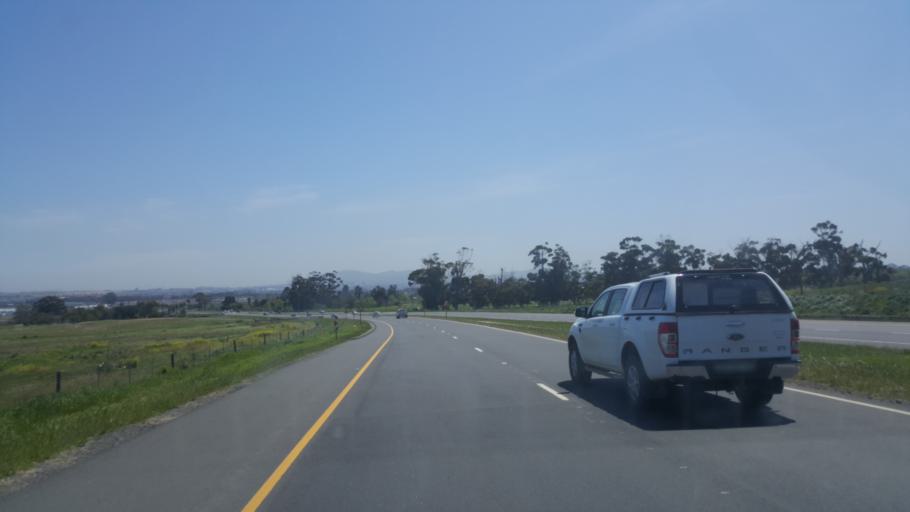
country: ZA
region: Western Cape
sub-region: City of Cape Town
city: Kraaifontein
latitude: -33.9542
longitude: 18.7187
